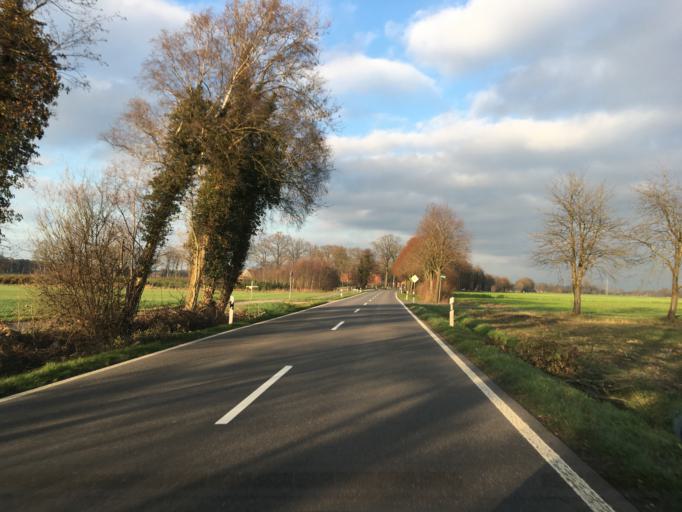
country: DE
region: North Rhine-Westphalia
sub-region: Regierungsbezirk Munster
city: Ahaus
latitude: 52.1344
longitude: 7.0068
